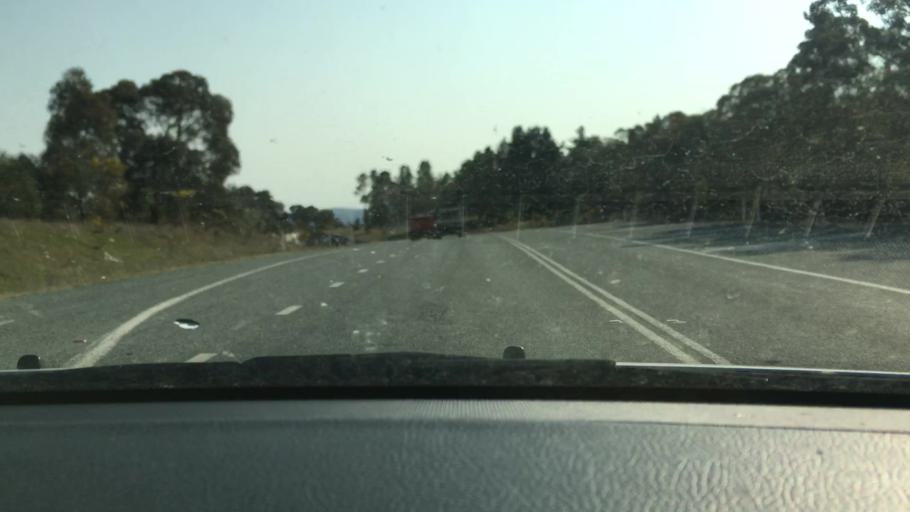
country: AU
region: New South Wales
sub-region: Queanbeyan
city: Queanbeyan
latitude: -35.4031
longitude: 149.2300
